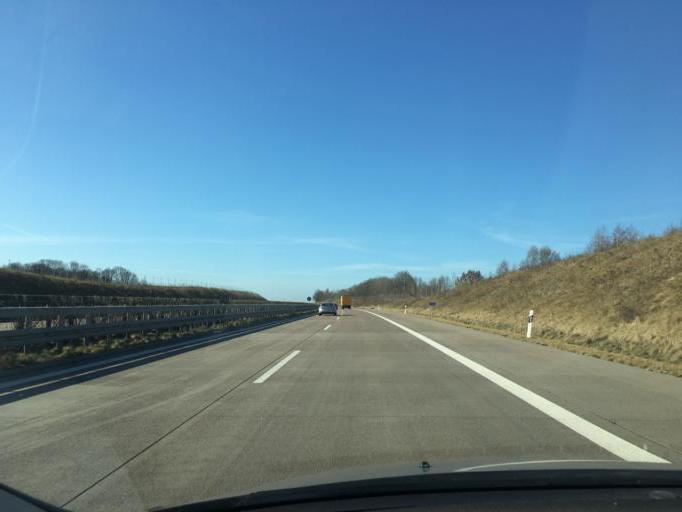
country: DE
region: Saxony
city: Penig
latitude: 50.9704
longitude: 12.6927
